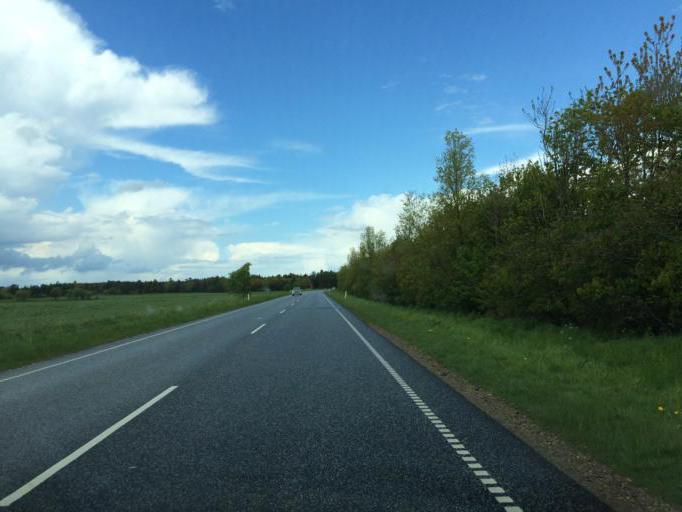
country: DK
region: North Denmark
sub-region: Vesthimmerland Kommune
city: Farso
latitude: 56.6135
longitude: 9.3509
